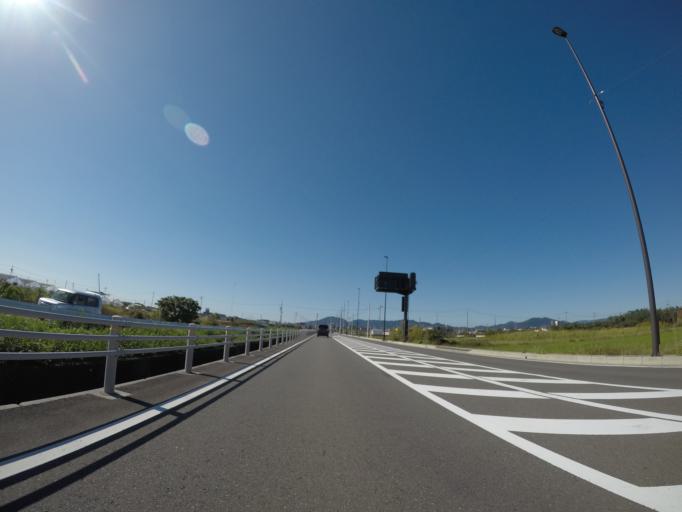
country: JP
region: Shizuoka
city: Shizuoka-shi
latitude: 34.9582
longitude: 138.4246
